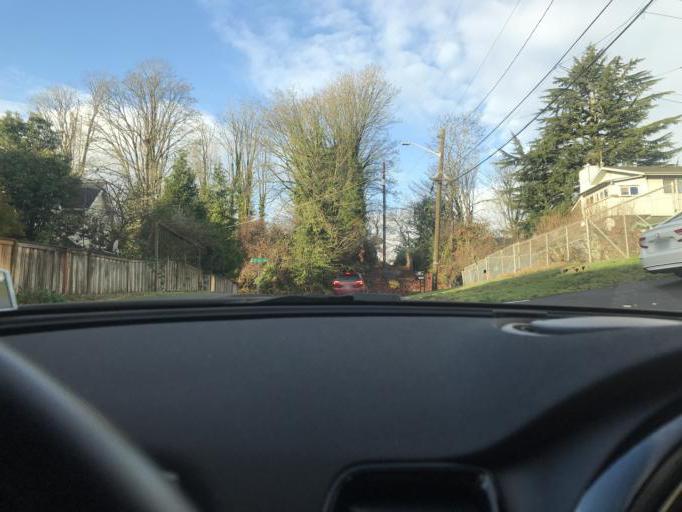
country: US
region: Washington
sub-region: King County
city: Riverton
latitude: 47.5424
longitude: -122.2895
